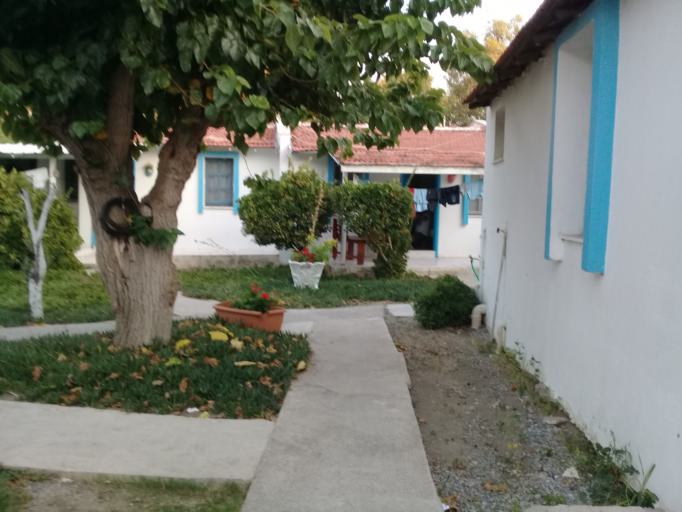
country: TR
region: Izmir
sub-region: Seferihisar
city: Seferhisar
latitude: 38.1685
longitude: 26.8075
